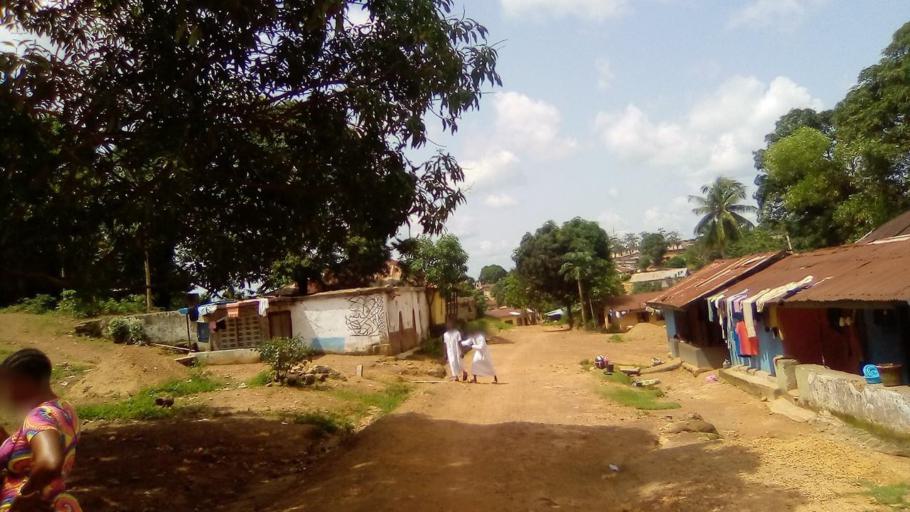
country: SL
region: Southern Province
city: Bo
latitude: 7.9661
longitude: -11.7297
